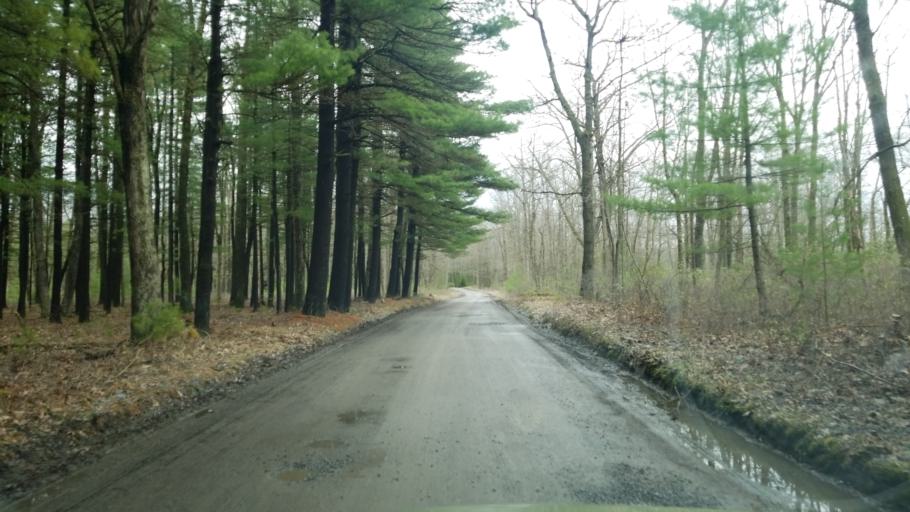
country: US
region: Pennsylvania
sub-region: Clearfield County
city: Shiloh
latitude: 41.1689
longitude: -78.2772
